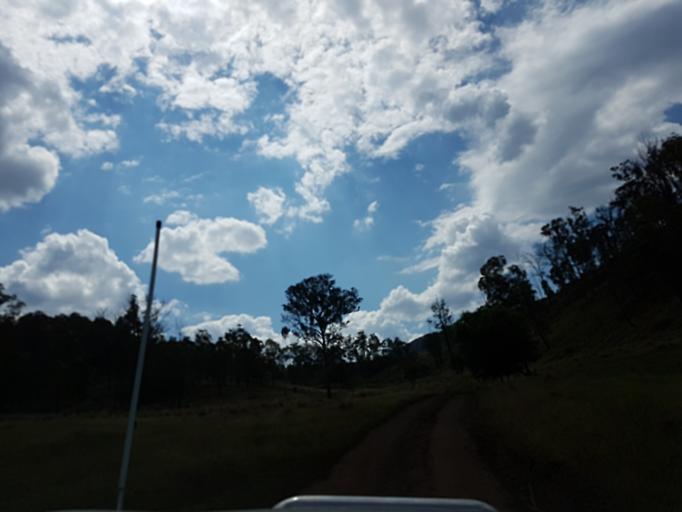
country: AU
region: Victoria
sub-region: East Gippsland
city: Lakes Entrance
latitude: -37.4004
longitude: 148.3288
